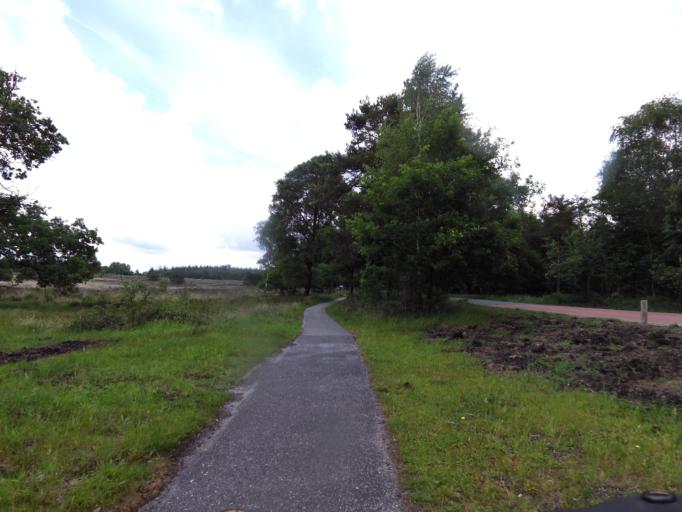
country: NL
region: Gelderland
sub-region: Gemeente Nunspeet
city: Nunspeet
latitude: 52.3282
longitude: 5.7707
